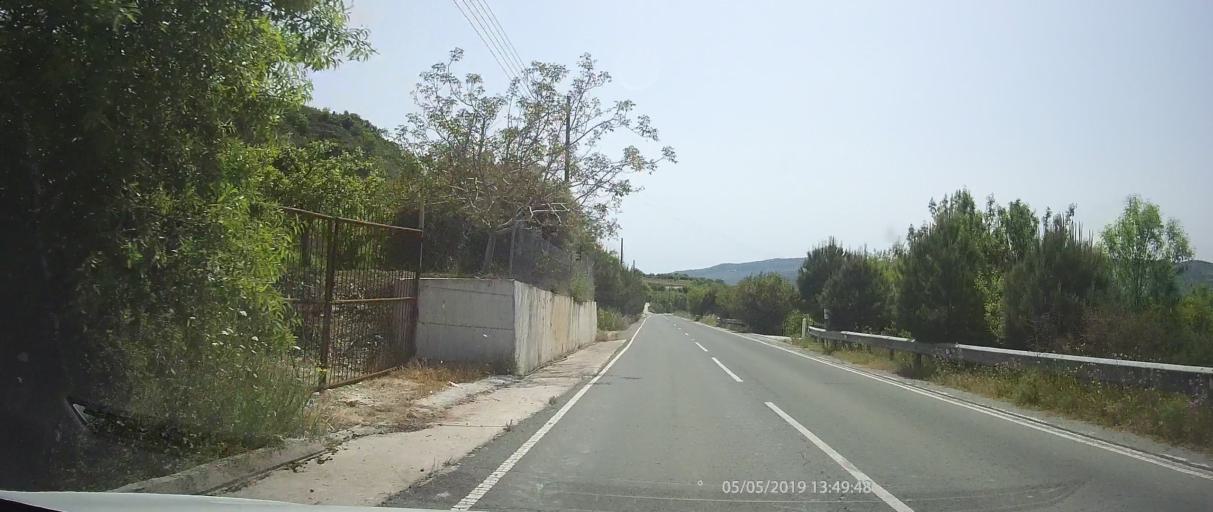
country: CY
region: Limassol
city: Pachna
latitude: 34.8462
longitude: 32.7460
